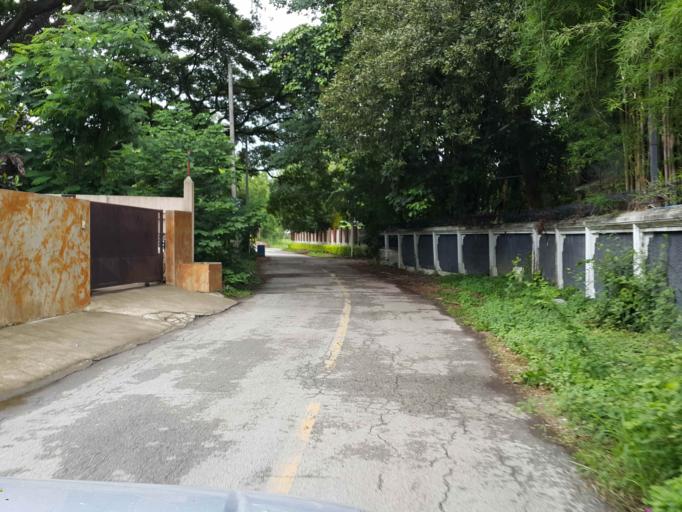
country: TH
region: Chiang Mai
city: Chiang Mai
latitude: 18.8172
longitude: 98.9949
